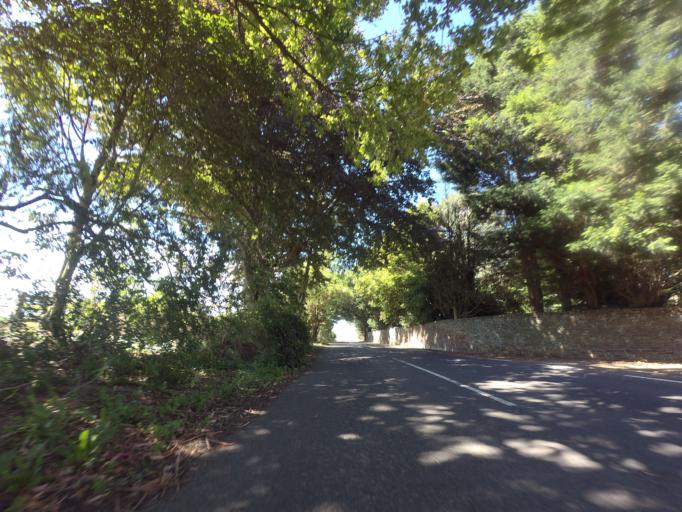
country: GB
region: England
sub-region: Kent
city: Westgate on Sea
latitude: 51.3305
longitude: 1.3457
